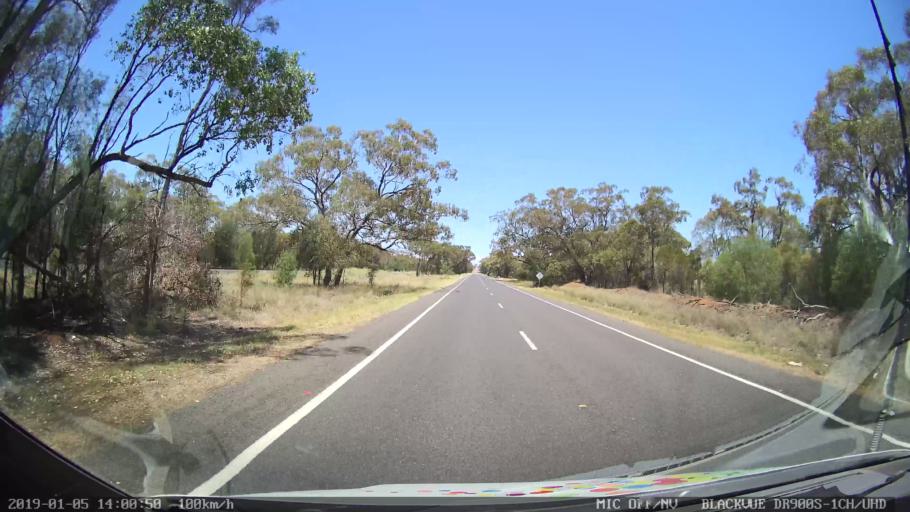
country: AU
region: New South Wales
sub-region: Gunnedah
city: Gunnedah
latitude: -31.1636
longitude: 150.3173
